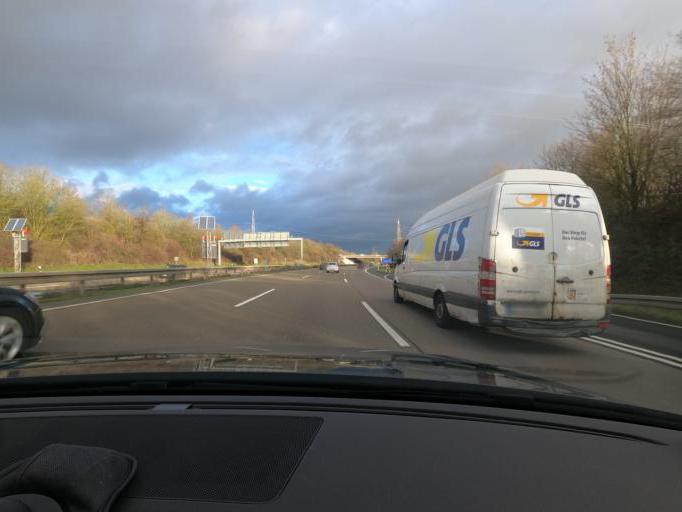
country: DE
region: Hesse
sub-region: Regierungsbezirk Darmstadt
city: Kriftel
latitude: 50.0940
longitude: 8.4835
